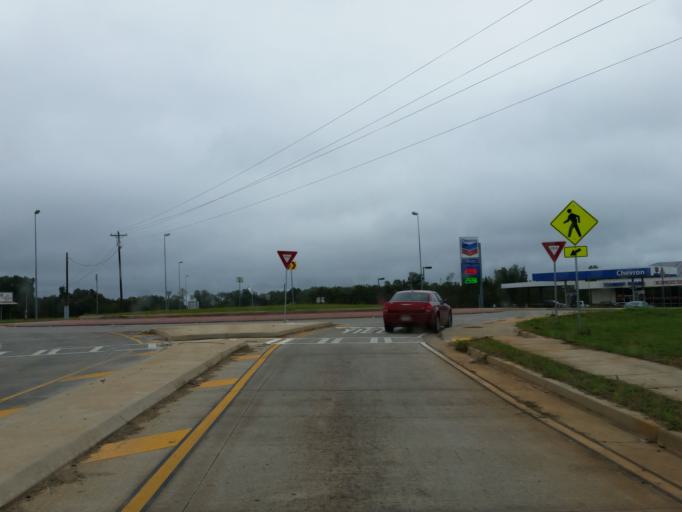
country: US
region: Georgia
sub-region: Crawford County
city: Roberta
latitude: 32.8801
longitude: -84.0900
